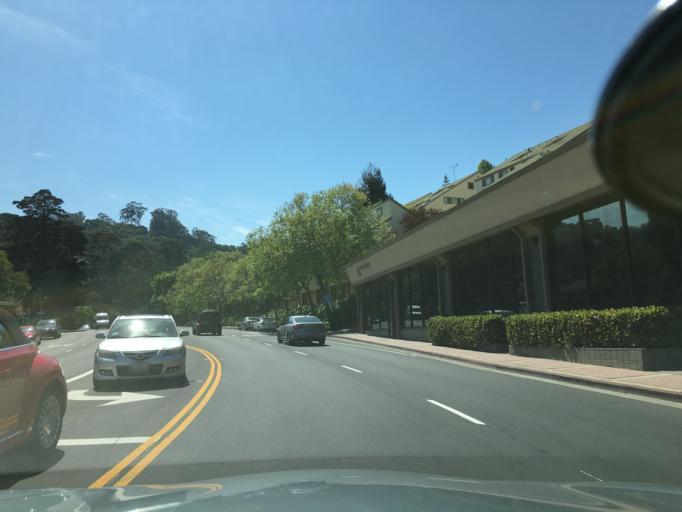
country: US
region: California
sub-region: San Mateo County
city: Belmont
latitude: 37.5192
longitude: -122.2774
